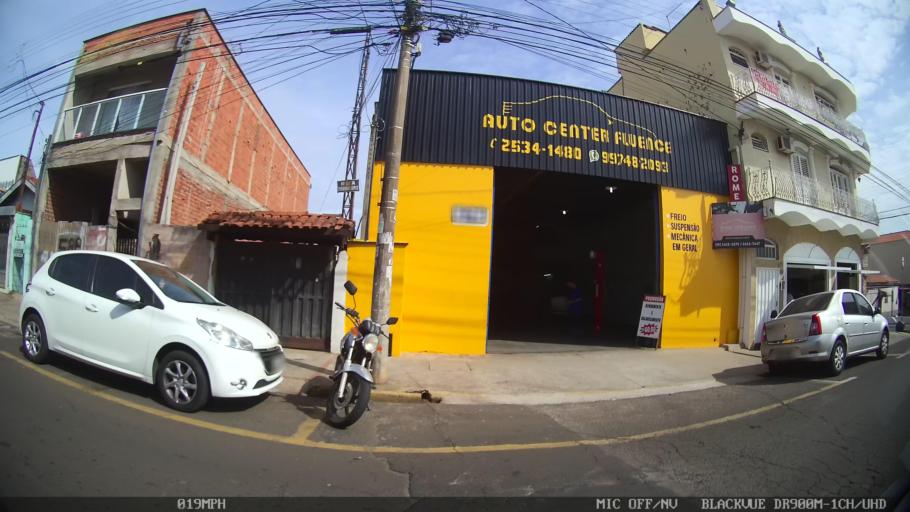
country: BR
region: Sao Paulo
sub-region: Piracicaba
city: Piracicaba
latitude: -22.7437
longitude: -47.6504
